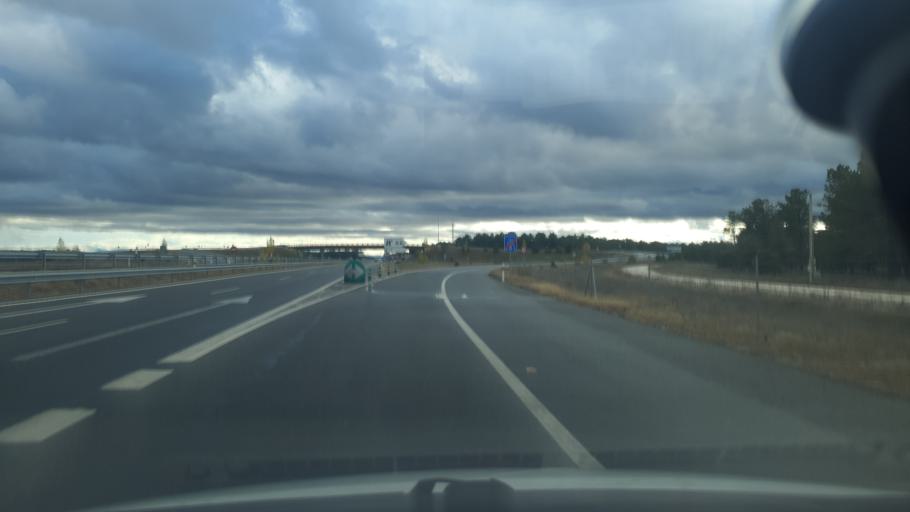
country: ES
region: Castille and Leon
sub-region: Provincia de Segovia
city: Sanchonuno
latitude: 41.2978
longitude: -4.3010
